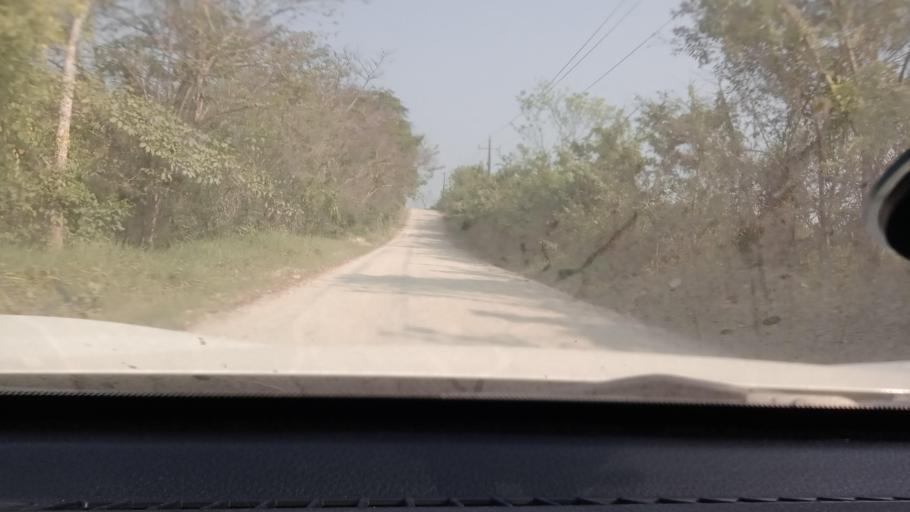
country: MX
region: Tabasco
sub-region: Huimanguillo
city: Francisco Rueda
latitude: 17.6140
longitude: -93.9387
